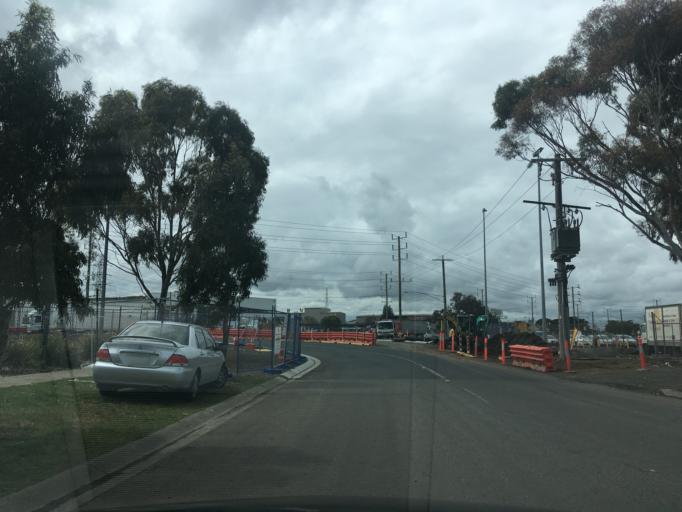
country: AU
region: Victoria
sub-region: Brimbank
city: Brooklyn
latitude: -37.8302
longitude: 144.8032
